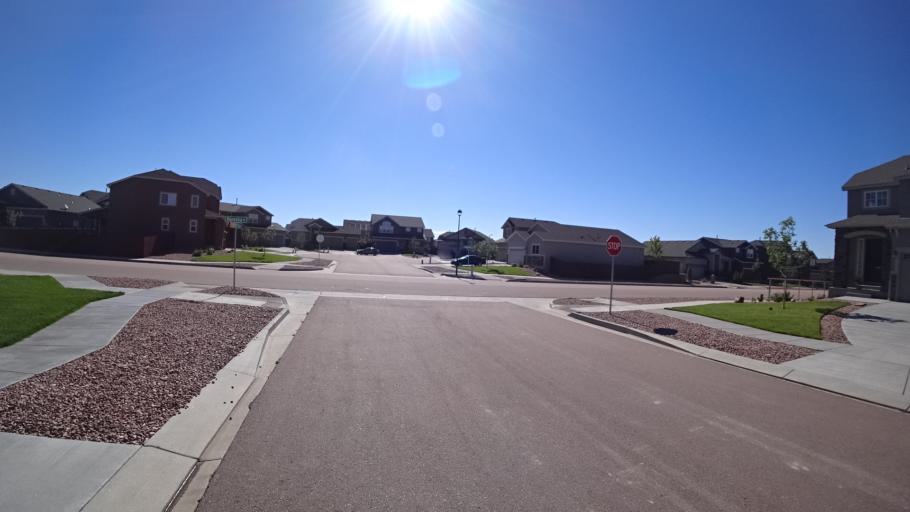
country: US
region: Colorado
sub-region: El Paso County
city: Black Forest
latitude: 38.9473
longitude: -104.6764
